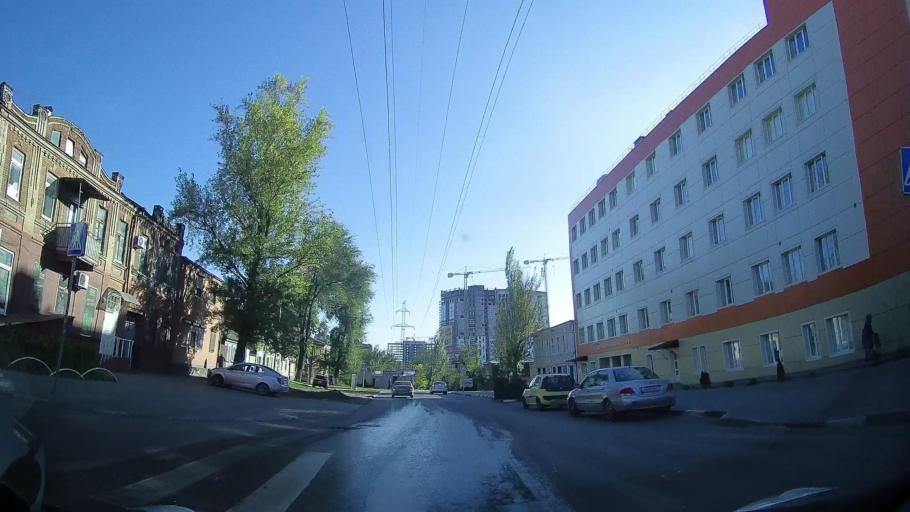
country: RU
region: Rostov
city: Rostov-na-Donu
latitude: 47.2292
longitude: 39.6904
